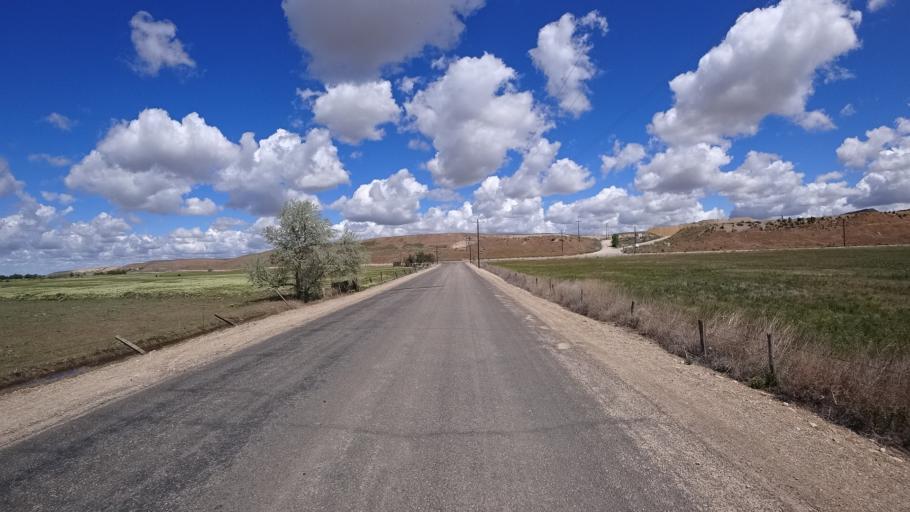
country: US
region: Idaho
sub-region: Ada County
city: Garden City
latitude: 43.4917
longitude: -116.2743
